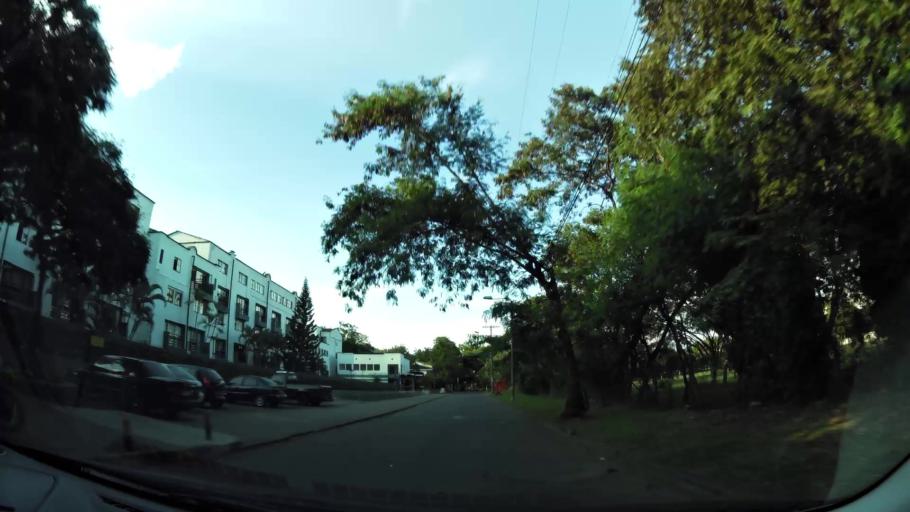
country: CO
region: Valle del Cauca
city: Cali
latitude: 3.4035
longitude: -76.5552
